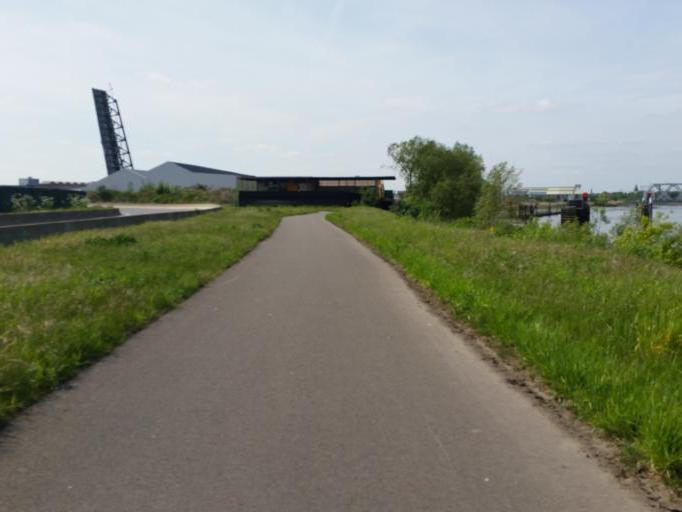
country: BE
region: Flanders
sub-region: Provincie Antwerpen
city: Boom
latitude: 51.0844
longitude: 4.3575
